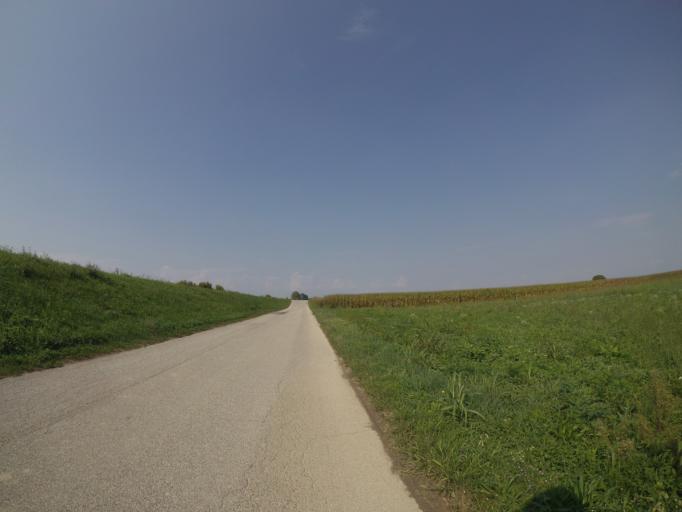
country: IT
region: Friuli Venezia Giulia
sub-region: Provincia di Udine
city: Camino al Tagliamento
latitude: 45.9396
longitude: 12.9192
